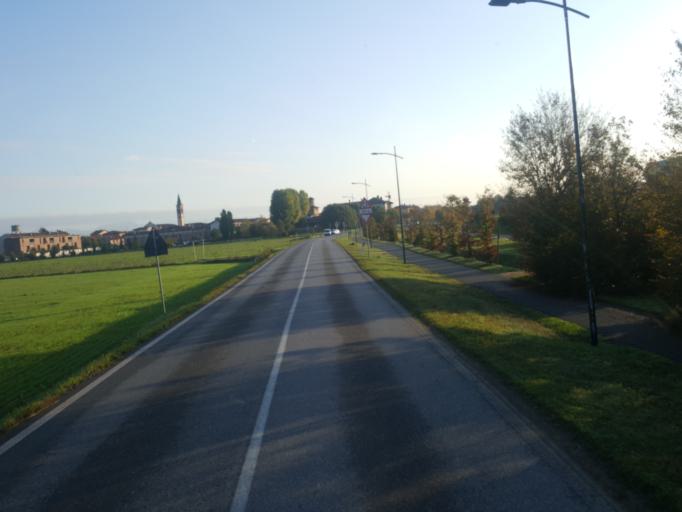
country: IT
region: Lombardy
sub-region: Provincia di Bergamo
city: Pagazzano
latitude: 45.5303
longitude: 9.6649
